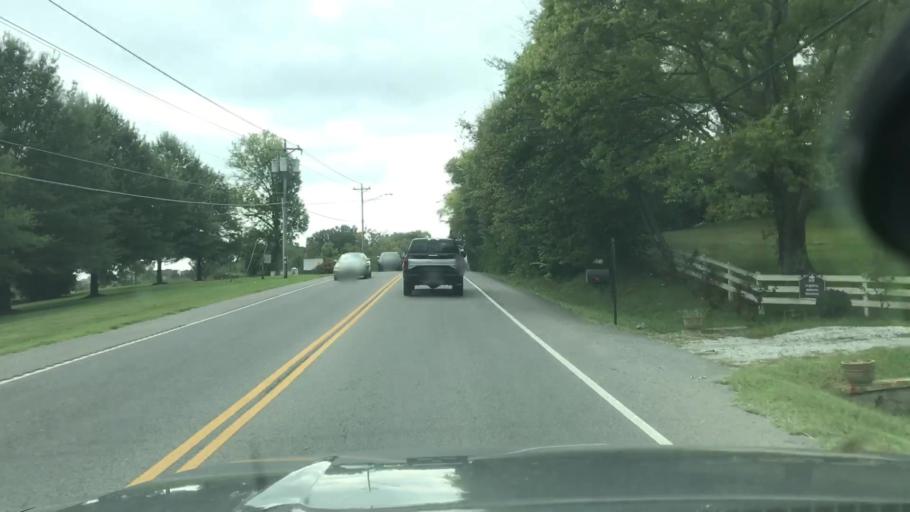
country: US
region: Tennessee
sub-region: Williamson County
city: Franklin
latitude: 35.9644
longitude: -86.8390
